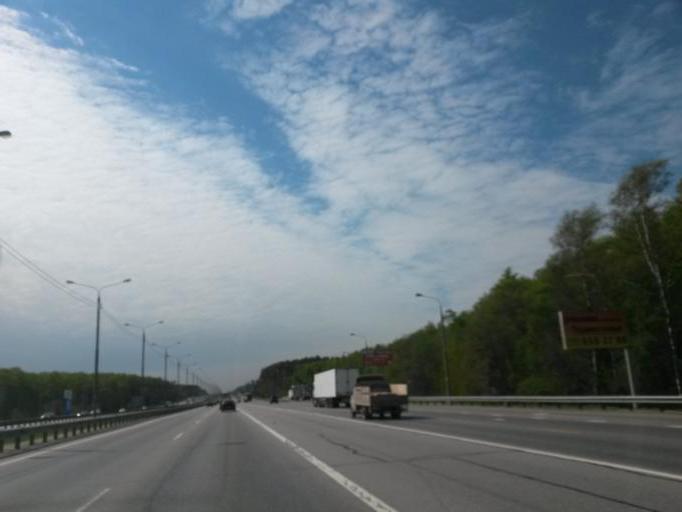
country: RU
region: Moskovskaya
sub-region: Podol'skiy Rayon
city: Podol'sk
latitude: 55.4272
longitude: 37.6126
